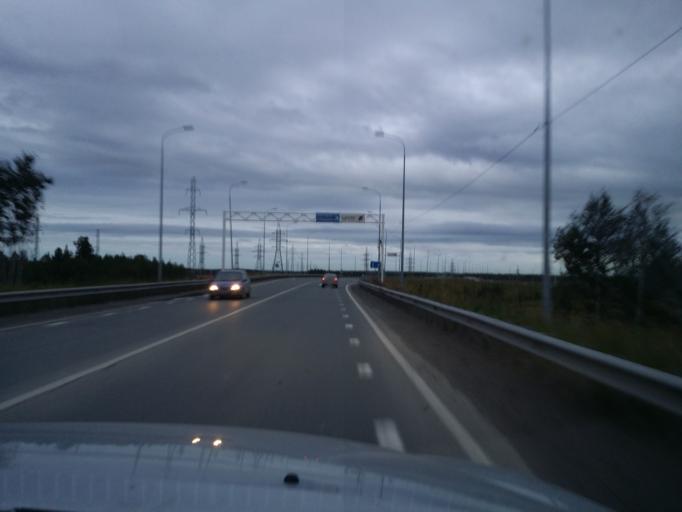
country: RU
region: Khanty-Mansiyskiy Avtonomnyy Okrug
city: Nizhnevartovsk
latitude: 60.9513
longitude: 76.6632
